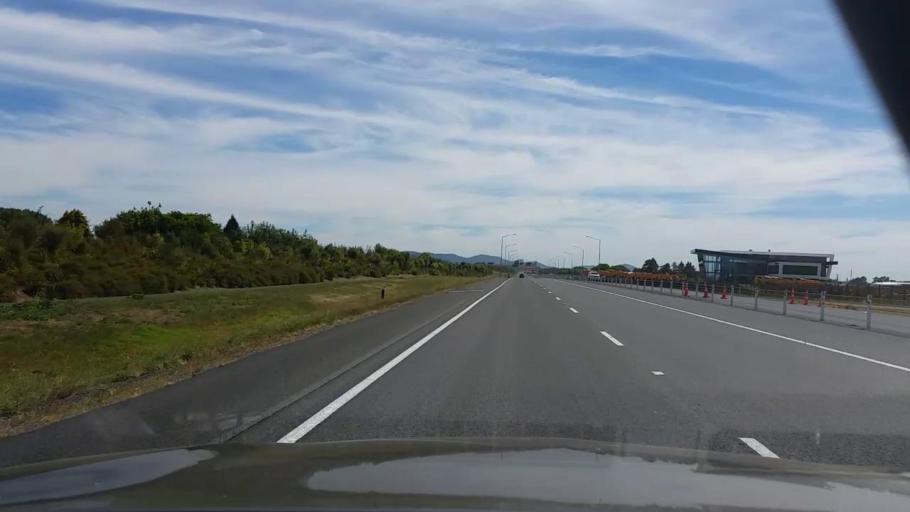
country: NZ
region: Waikato
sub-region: Hamilton City
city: Hamilton
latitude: -37.7424
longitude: 175.2135
